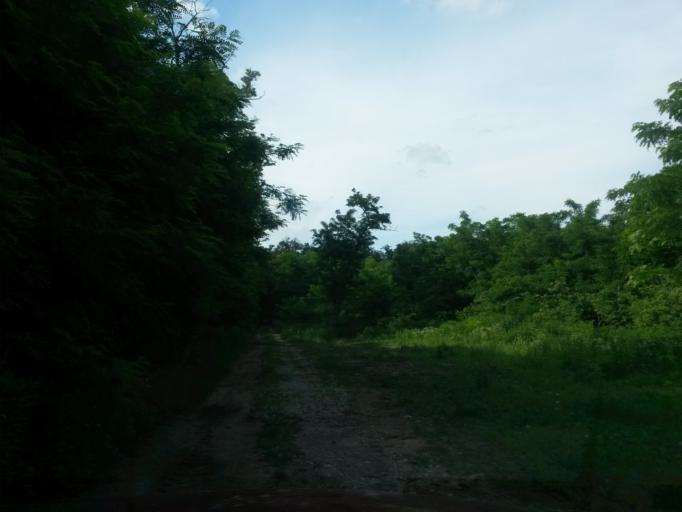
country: SK
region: Kosicky
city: Moldava nad Bodvou
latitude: 48.6102
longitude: 21.1133
